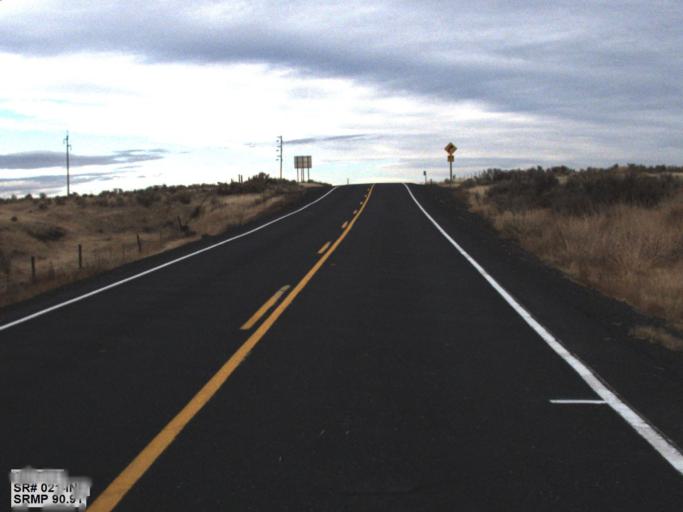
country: US
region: Washington
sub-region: Okanogan County
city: Coulee Dam
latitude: 47.7545
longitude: -118.7217
